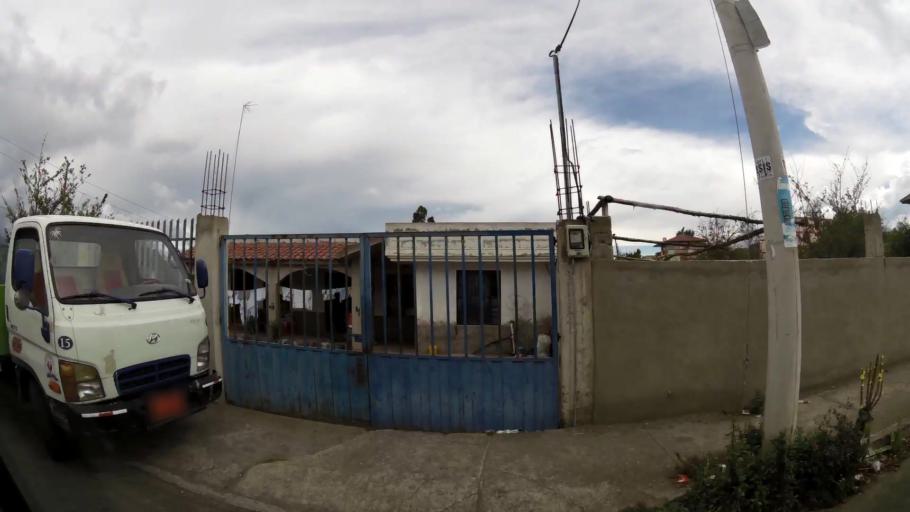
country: EC
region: Tungurahua
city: Ambato
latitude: -1.2806
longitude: -78.6290
